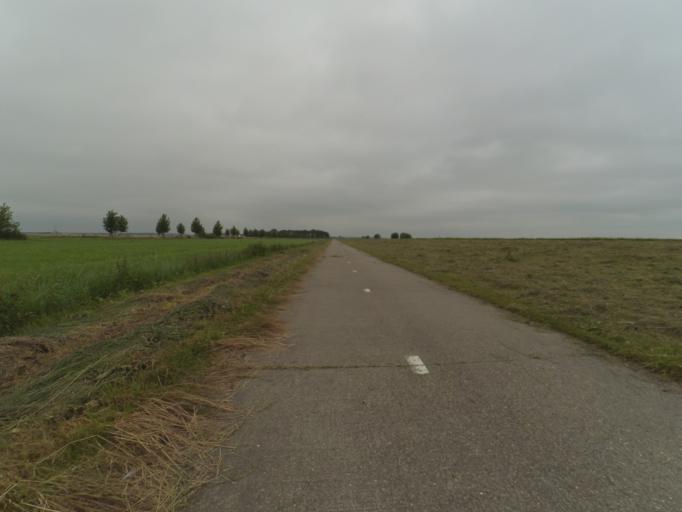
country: NL
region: Flevoland
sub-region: Gemeente Lelystad
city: Lelystad
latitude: 52.4235
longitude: 5.5151
